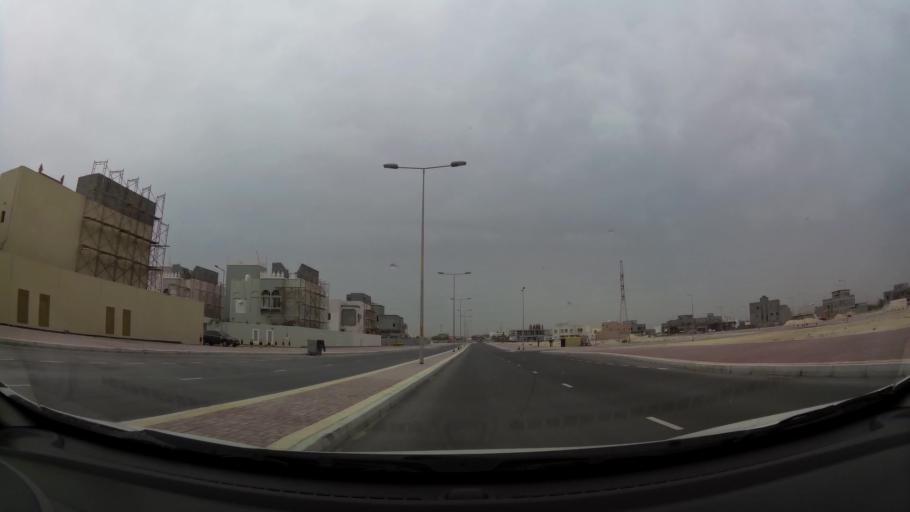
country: BH
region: Northern
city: Madinat `Isa
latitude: 26.1658
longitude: 50.5392
